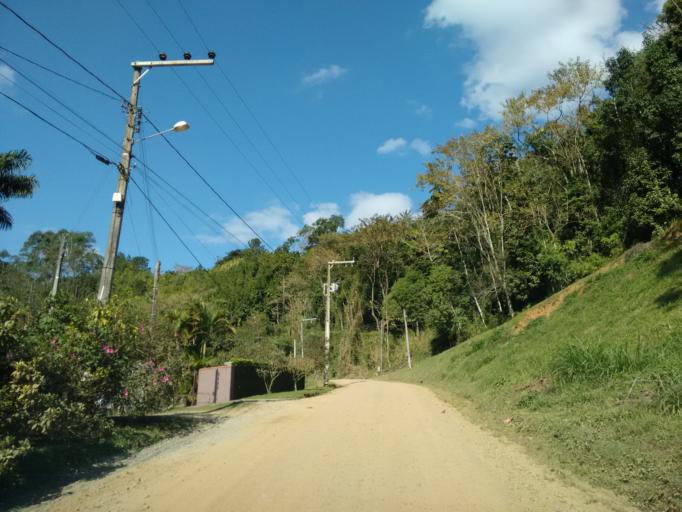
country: BR
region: Santa Catarina
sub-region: Pomerode
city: Pomerode
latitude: -26.7403
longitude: -49.1610
